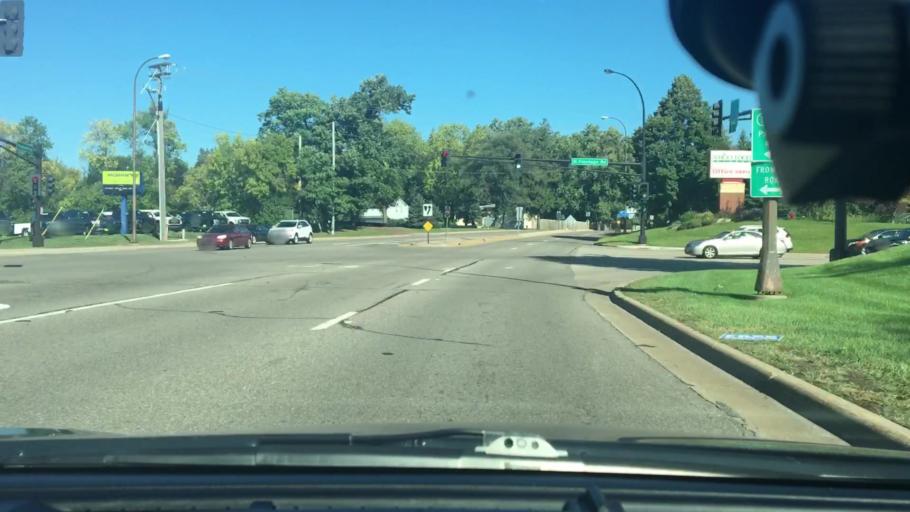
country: US
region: Minnesota
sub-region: Hennepin County
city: Minnetonka Mills
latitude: 44.9726
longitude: -93.4459
